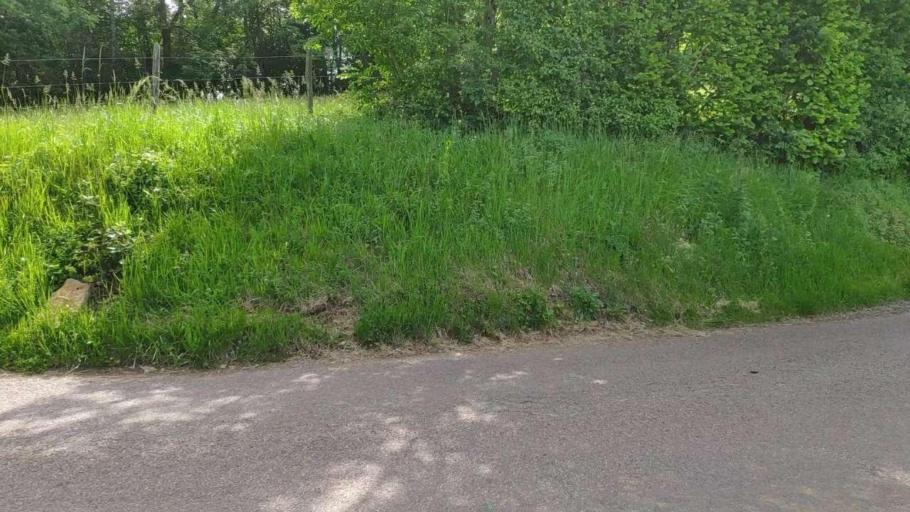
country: FR
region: Franche-Comte
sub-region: Departement du Jura
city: Poligny
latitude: 46.7755
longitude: 5.6295
